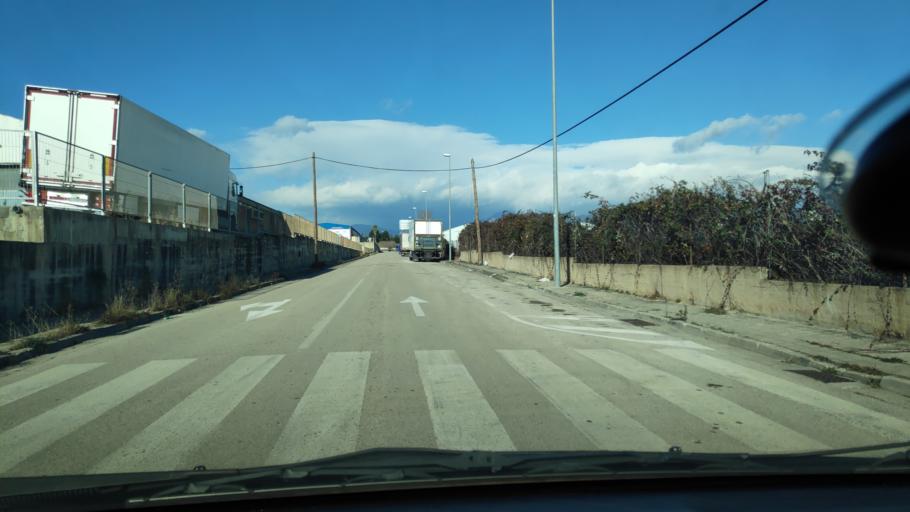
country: ES
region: Catalonia
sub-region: Provincia de Barcelona
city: Sant Quirze del Valles
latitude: 41.5394
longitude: 2.0793
